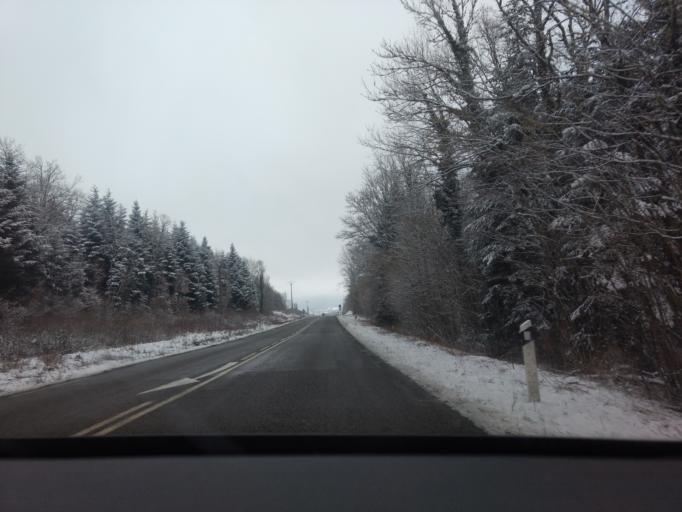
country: FR
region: Franche-Comte
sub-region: Departement du Jura
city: Champagnole
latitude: 46.7807
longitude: 5.8816
